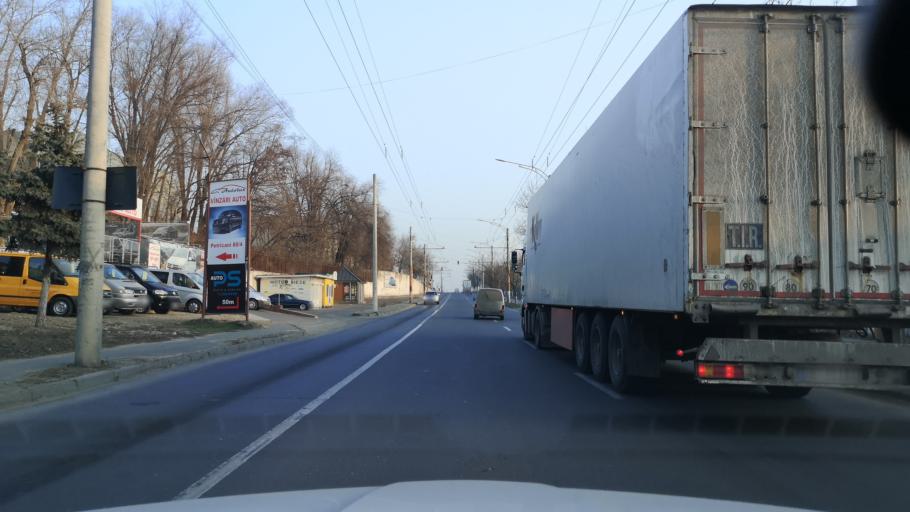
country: MD
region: Chisinau
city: Chisinau
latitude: 47.0473
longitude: 28.8275
